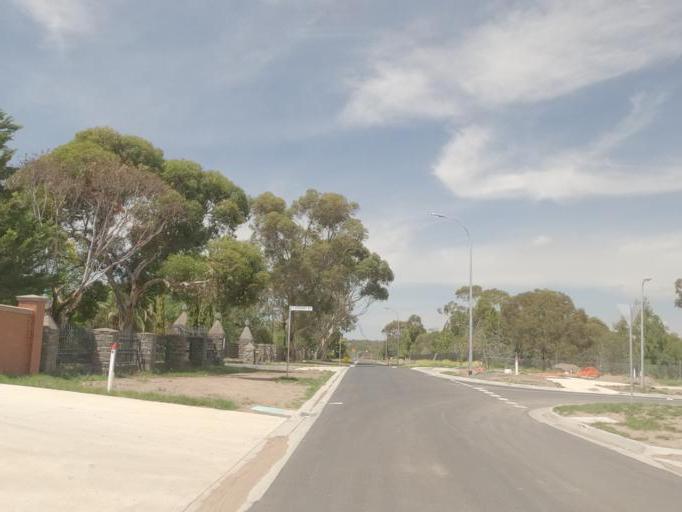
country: AU
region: Victoria
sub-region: Hume
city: Greenvale
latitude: -37.6373
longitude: 144.8755
